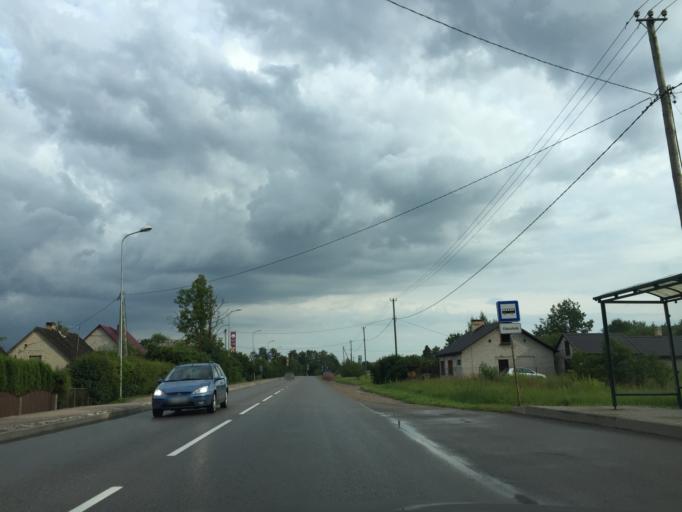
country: LV
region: Dobeles Rajons
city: Dobele
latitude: 56.6185
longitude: 23.2719
